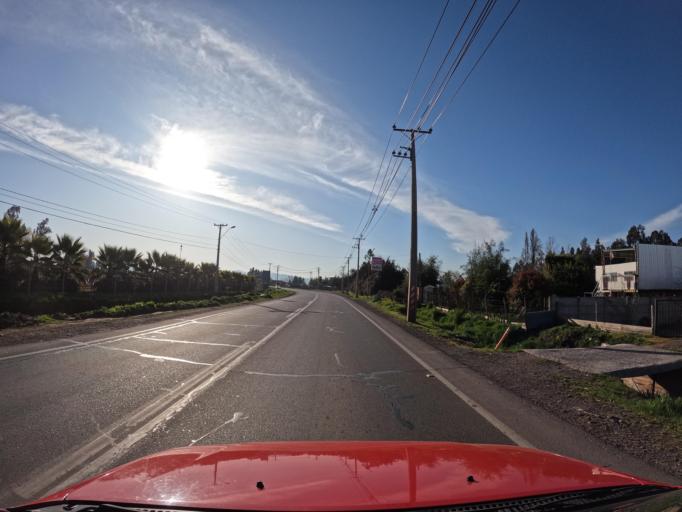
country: CL
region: Maule
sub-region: Provincia de Curico
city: Teno
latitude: -34.8601
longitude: -71.0961
